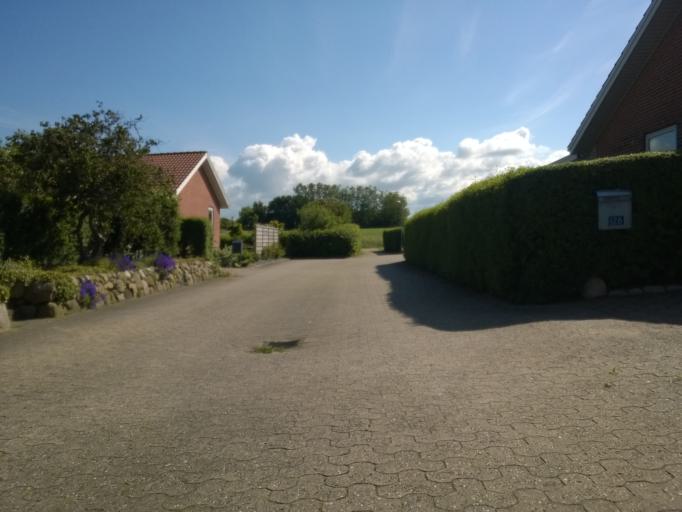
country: DK
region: Central Jutland
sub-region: Holstebro Kommune
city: Vinderup
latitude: 56.4751
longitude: 8.7746
